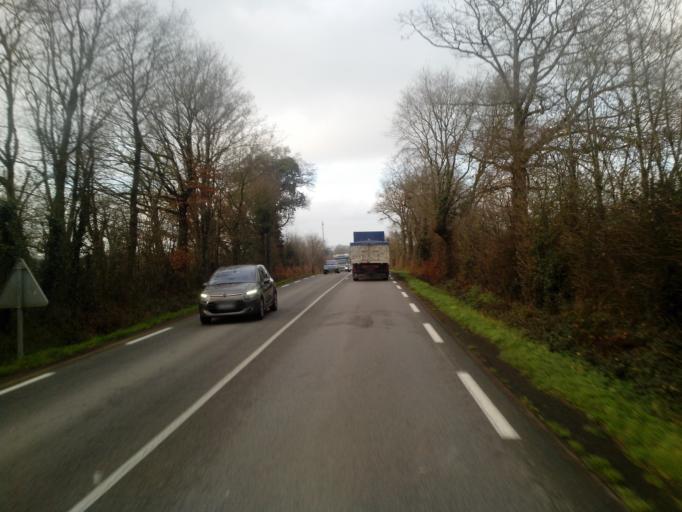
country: FR
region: Poitou-Charentes
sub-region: Departement des Deux-Sevres
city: Chiche
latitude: 46.7673
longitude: -0.3156
